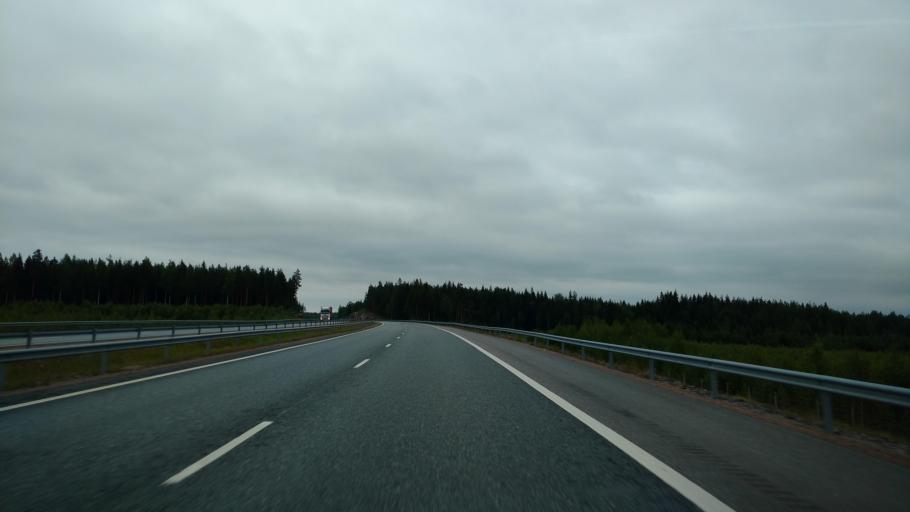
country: FI
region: Varsinais-Suomi
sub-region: Salo
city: Kiikala
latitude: 60.3830
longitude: 23.4969
